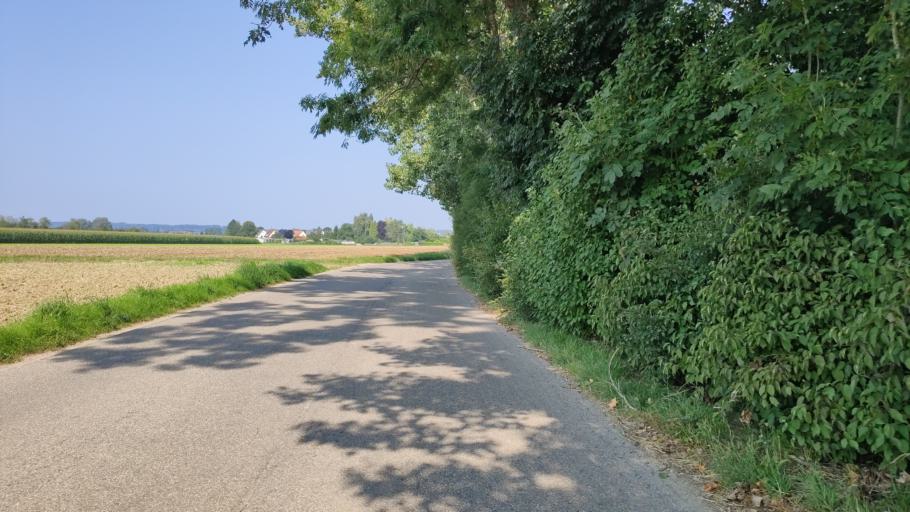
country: DE
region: Bavaria
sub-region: Swabia
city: Bobingen
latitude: 48.2590
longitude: 10.8383
